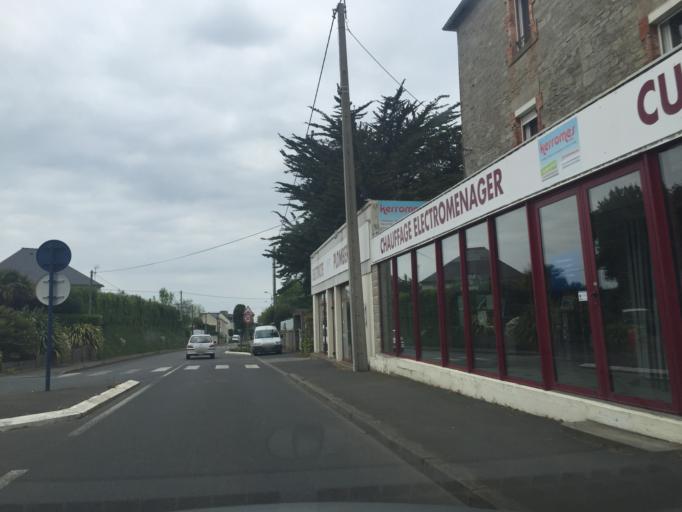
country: FR
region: Brittany
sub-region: Departement des Cotes-d'Armor
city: Saint-Cast-le-Guildo
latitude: 48.6203
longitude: -2.2644
